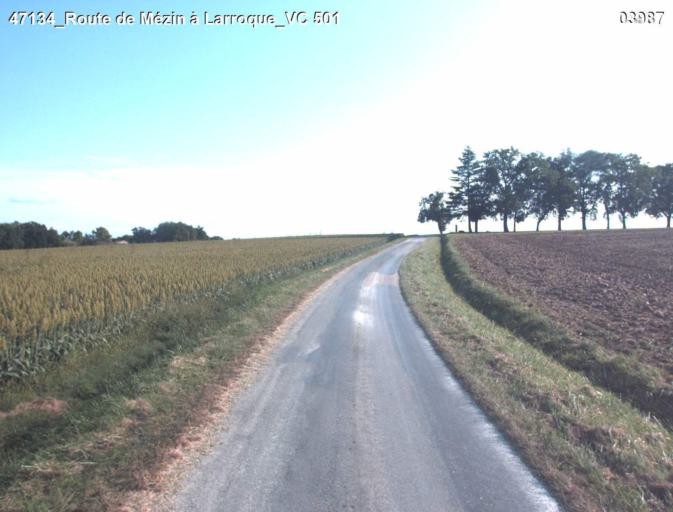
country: FR
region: Aquitaine
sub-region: Departement du Lot-et-Garonne
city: Mezin
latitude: 44.0301
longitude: 0.2679
